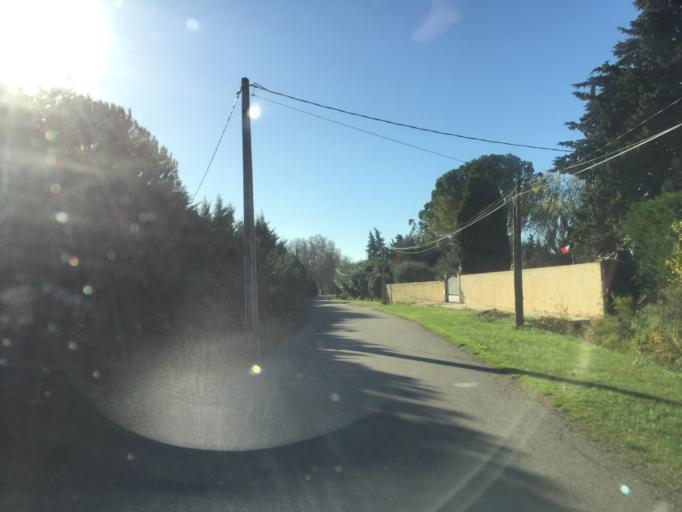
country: FR
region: Provence-Alpes-Cote d'Azur
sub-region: Departement du Vaucluse
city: Bedarrides
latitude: 44.0515
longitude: 4.9030
